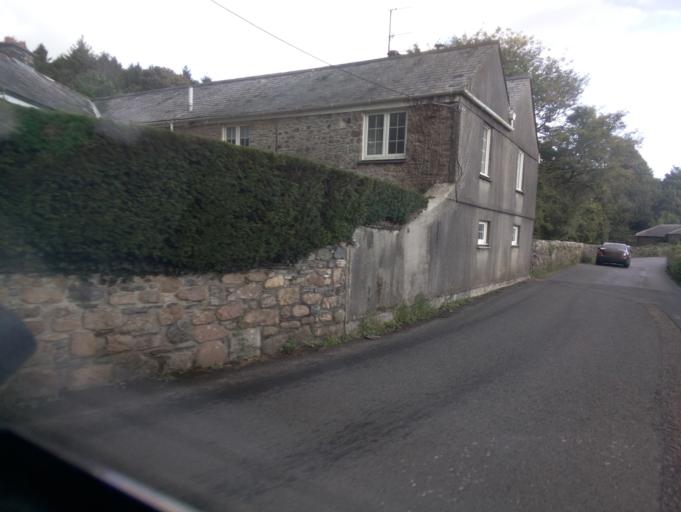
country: GB
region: England
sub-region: Devon
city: Ivybridge
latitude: 50.3741
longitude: -3.9133
